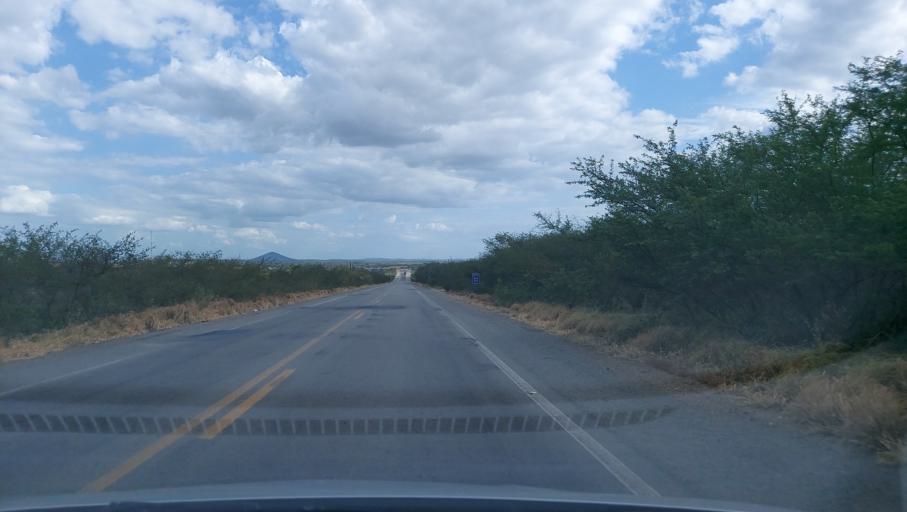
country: BR
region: Bahia
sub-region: Castro Alves
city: Castro Alves
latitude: -12.5757
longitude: -39.5256
